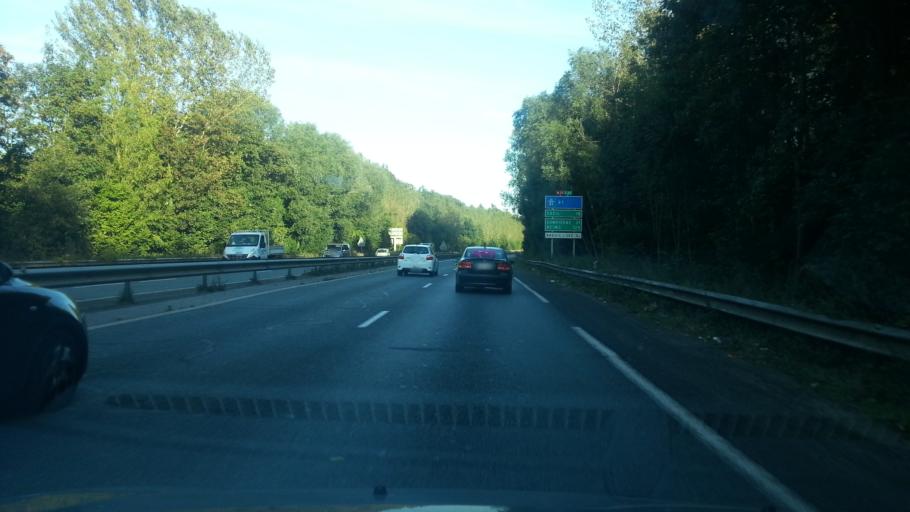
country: FR
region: Picardie
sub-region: Departement de l'Oise
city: Fitz-James
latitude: 49.3884
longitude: 2.4190
